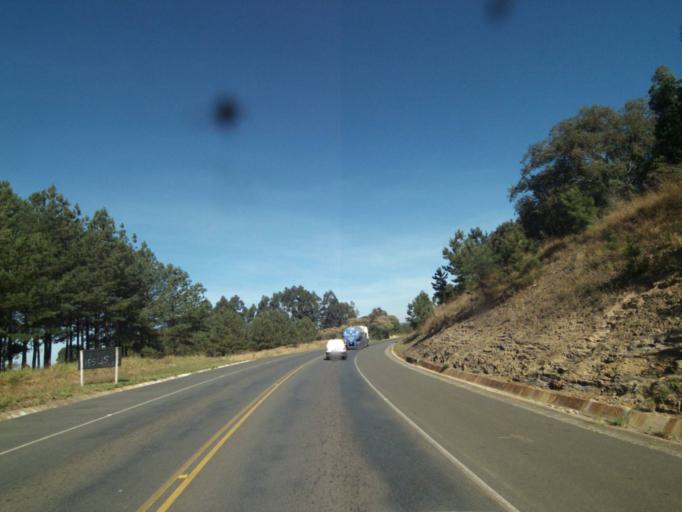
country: BR
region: Parana
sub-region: Tibagi
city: Tibagi
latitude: -24.5033
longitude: -50.4414
